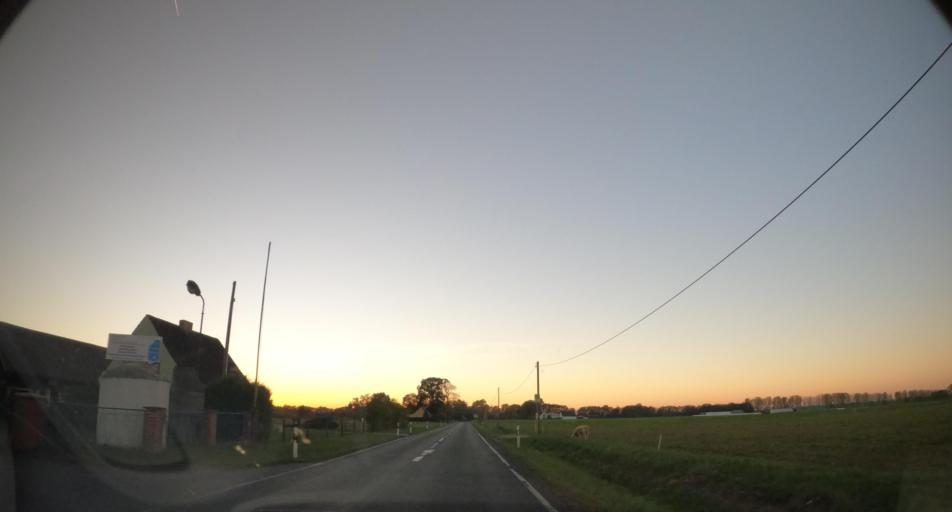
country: DE
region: Mecklenburg-Vorpommern
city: Ducherow
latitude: 53.7787
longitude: 13.8763
